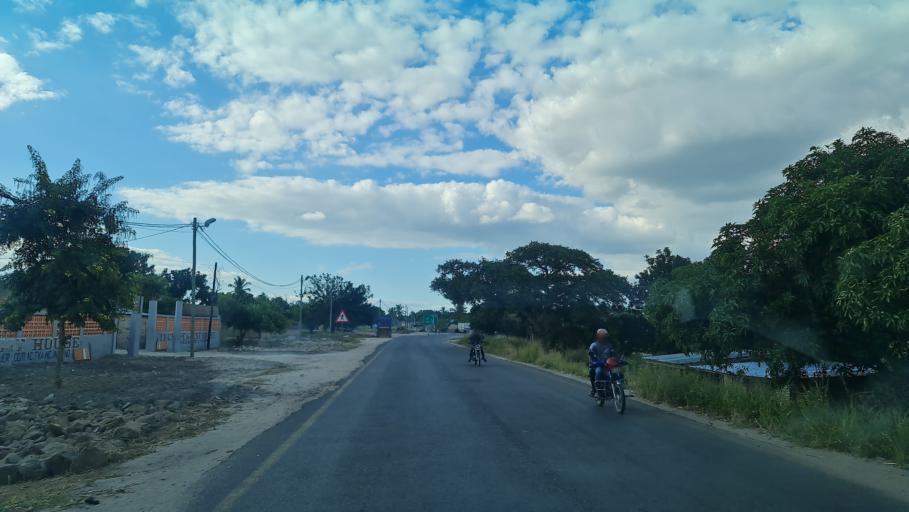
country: MZ
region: Manica
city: Chimoio
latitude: -19.2136
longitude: 33.9238
